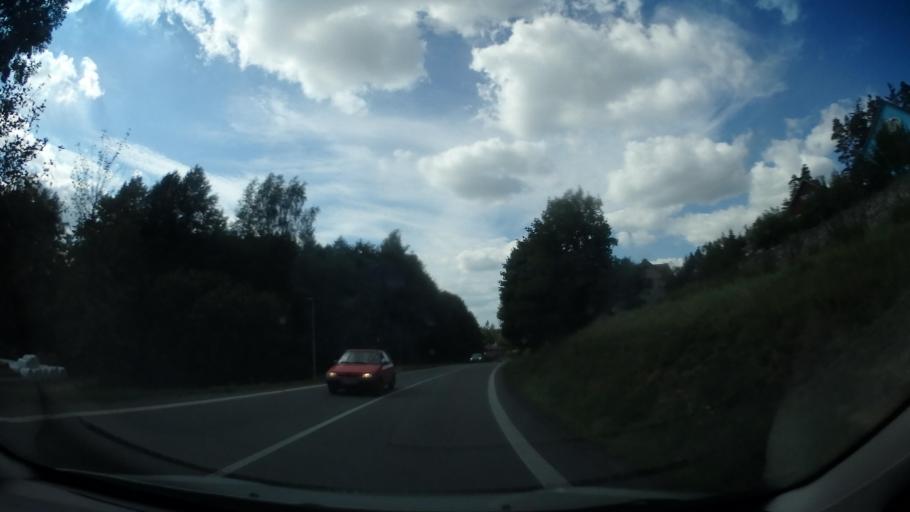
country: CZ
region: Vysocina
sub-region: Okres Zd'ar nad Sazavou
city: Nove Veseli
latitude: 49.5586
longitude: 15.8687
